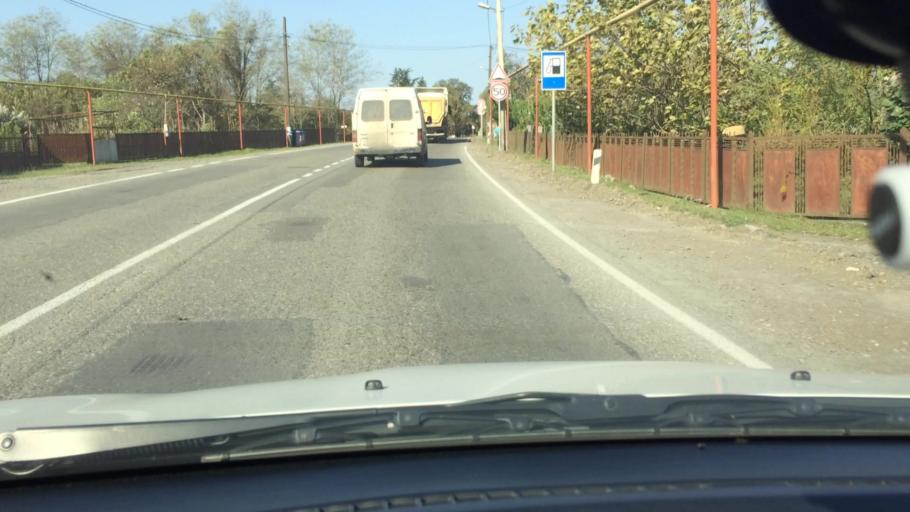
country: GE
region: Guria
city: Lanchkhuti
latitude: 42.0750
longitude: 42.0593
